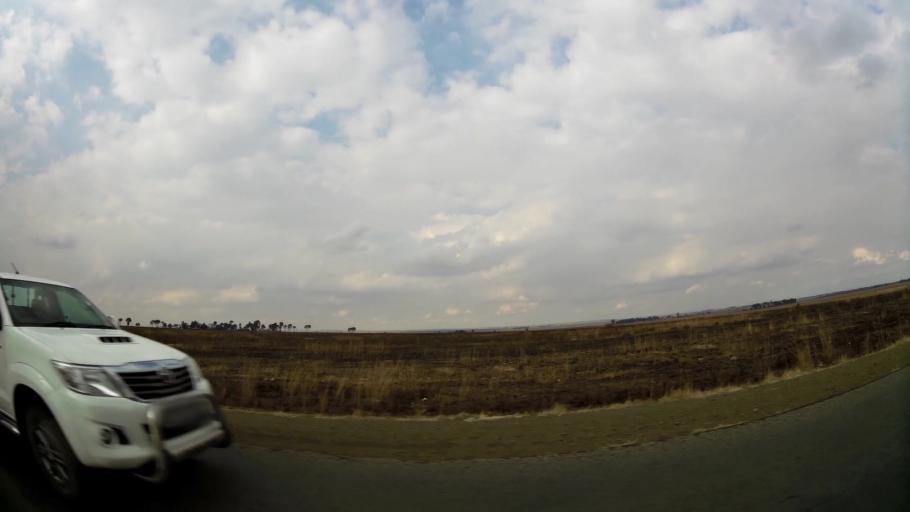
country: ZA
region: Orange Free State
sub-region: Fezile Dabi District Municipality
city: Sasolburg
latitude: -26.8792
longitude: 27.8863
